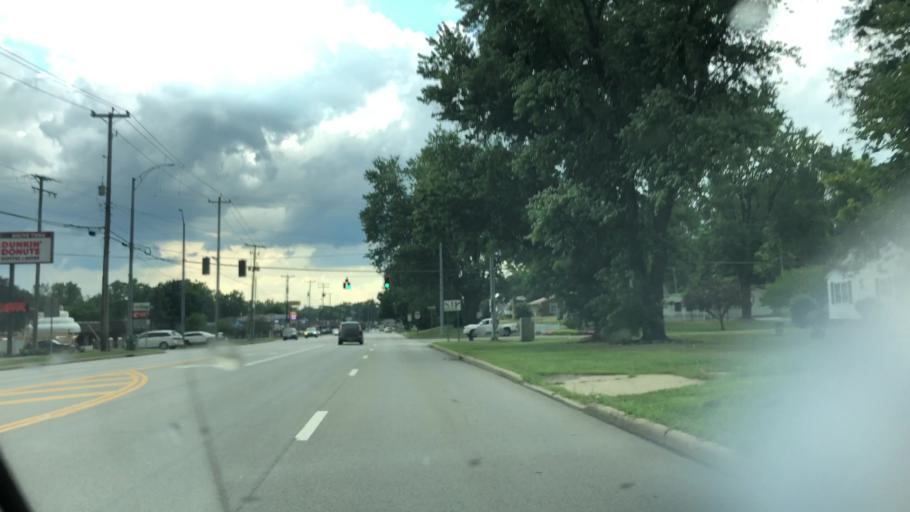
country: US
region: Ohio
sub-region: Stark County
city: North Canton
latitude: 40.8519
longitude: -81.4477
